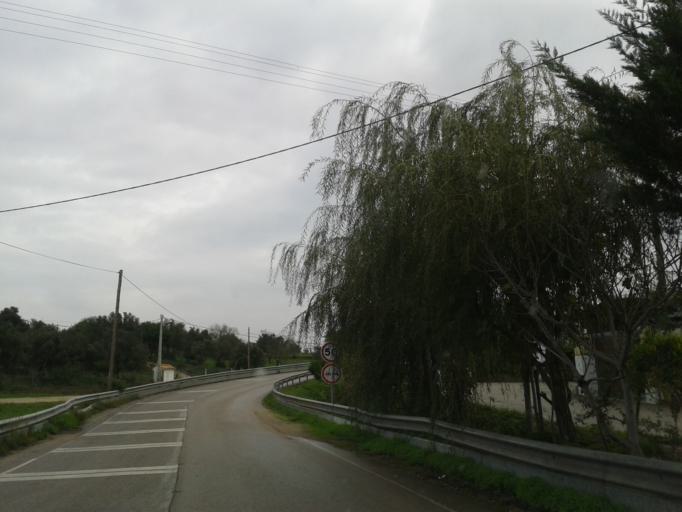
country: PT
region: Faro
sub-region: Loule
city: Boliqueime
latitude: 37.1148
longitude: -8.1872
